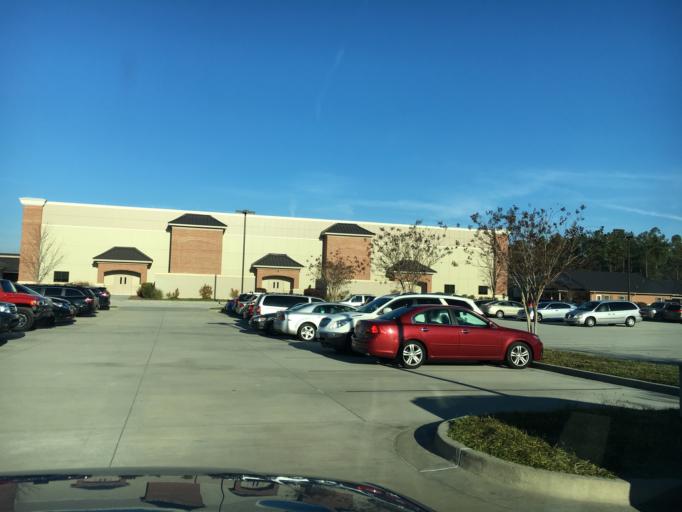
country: US
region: South Carolina
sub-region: Orangeburg County
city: Brookdale
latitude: 33.5242
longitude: -80.7928
